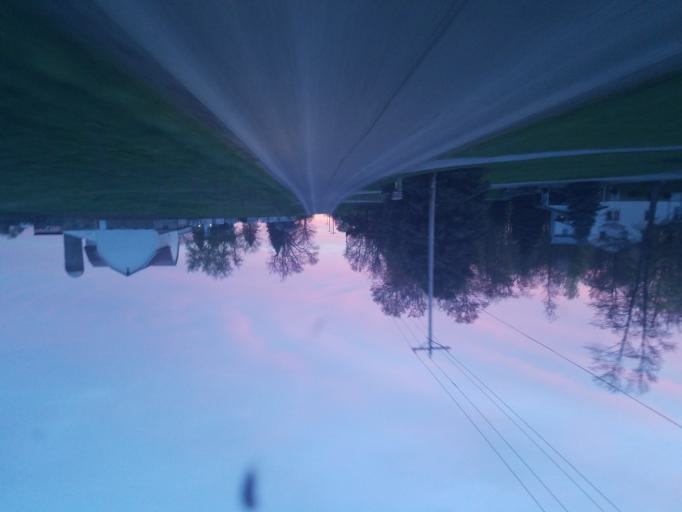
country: US
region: Ohio
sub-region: Wayne County
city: Apple Creek
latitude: 40.6998
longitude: -81.8229
